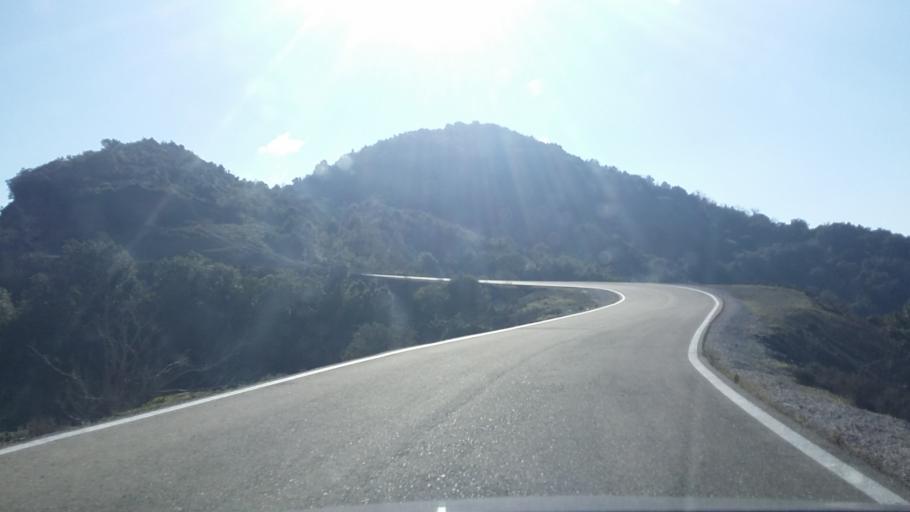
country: GR
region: West Greece
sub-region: Nomos Aitolias kai Akarnanias
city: Krikellos
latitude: 38.9908
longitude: 21.2776
